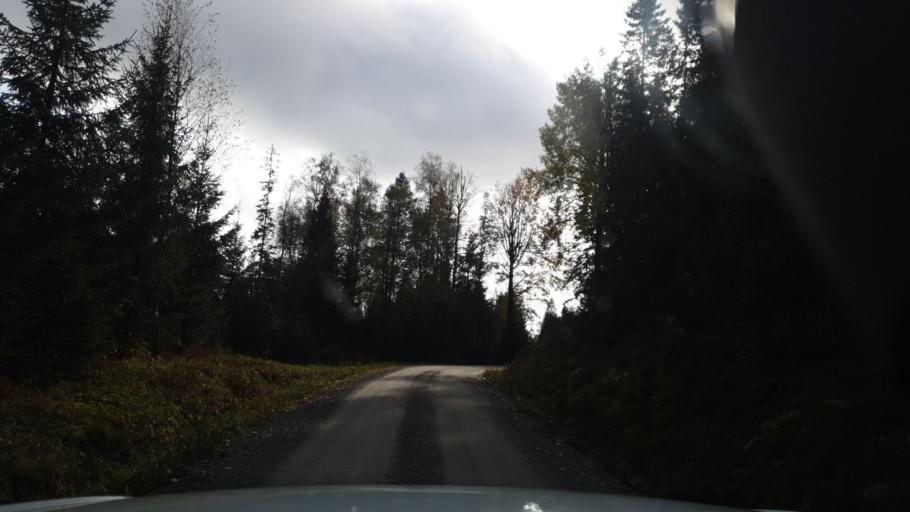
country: SE
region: Vaermland
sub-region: Arvika Kommun
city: Arvika
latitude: 59.5411
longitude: 12.4427
